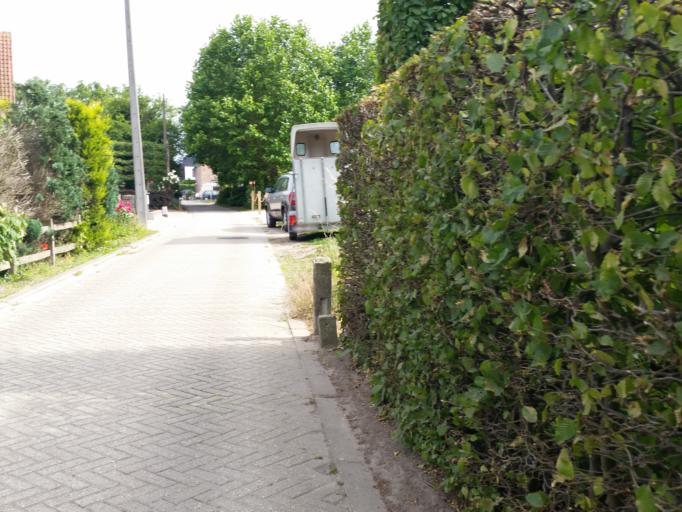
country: BE
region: Flanders
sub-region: Provincie Antwerpen
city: Puurs
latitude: 51.1025
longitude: 4.3016
